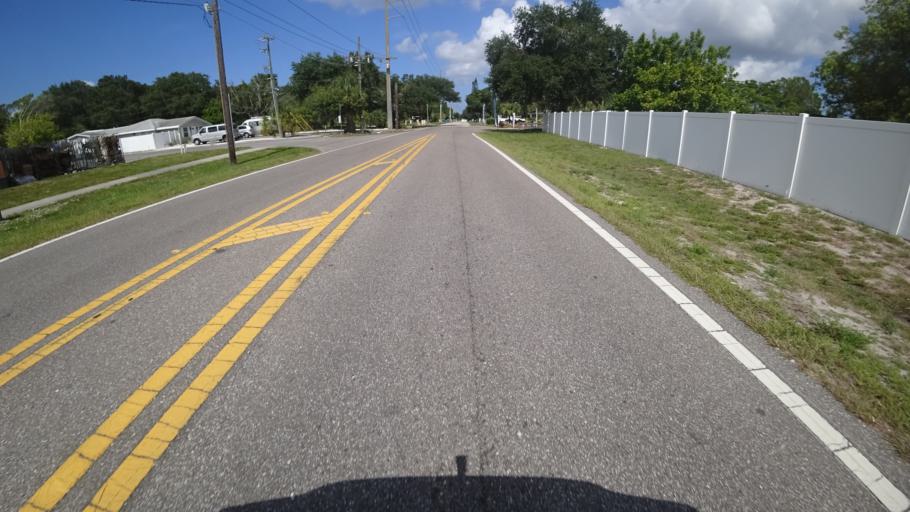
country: US
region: Florida
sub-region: Manatee County
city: Samoset
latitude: 27.4513
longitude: -82.5483
